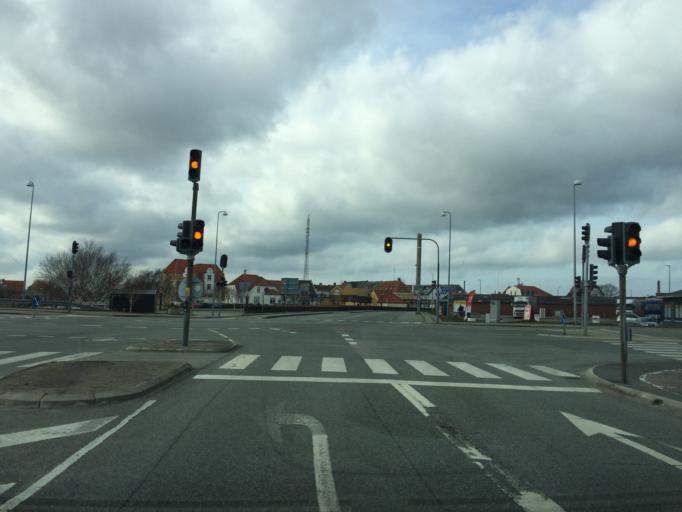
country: DK
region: Central Jutland
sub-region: Norddjurs Kommune
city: Grenaa
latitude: 56.4074
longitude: 10.9218
